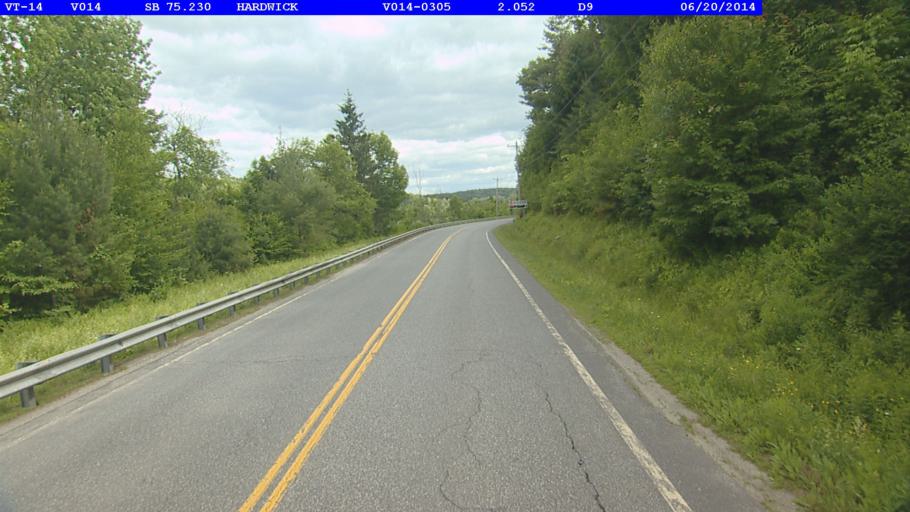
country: US
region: Vermont
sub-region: Caledonia County
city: Hardwick
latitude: 44.5238
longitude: -72.3751
